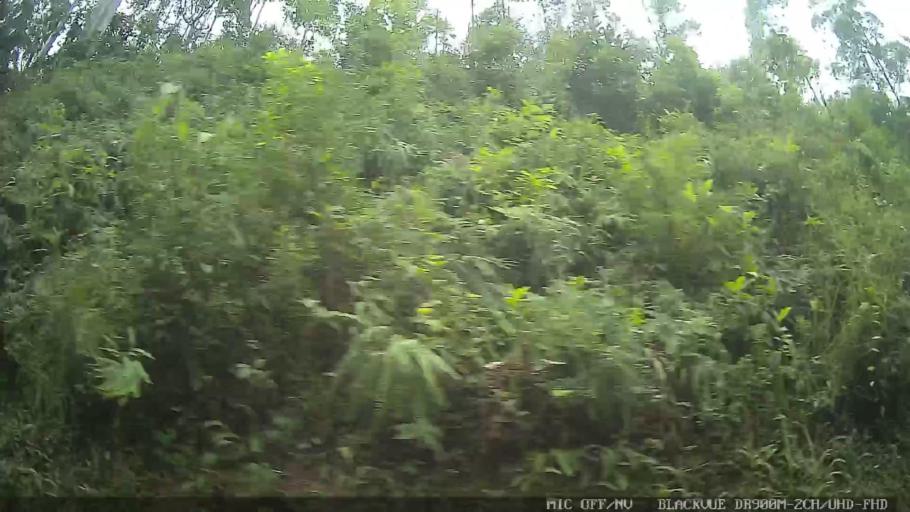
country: BR
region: Sao Paulo
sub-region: Caraguatatuba
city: Caraguatatuba
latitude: -23.5557
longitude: -45.6391
